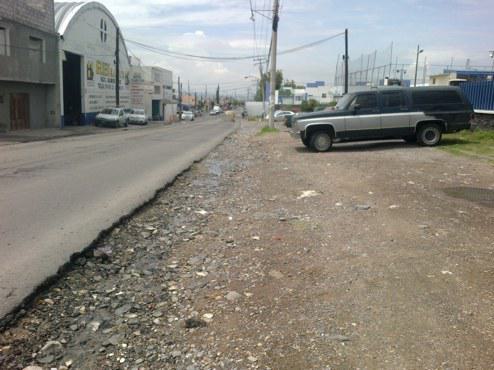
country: MX
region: Queretaro
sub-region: Queretaro
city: Sergio Villasenor
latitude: 20.6289
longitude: -100.3992
